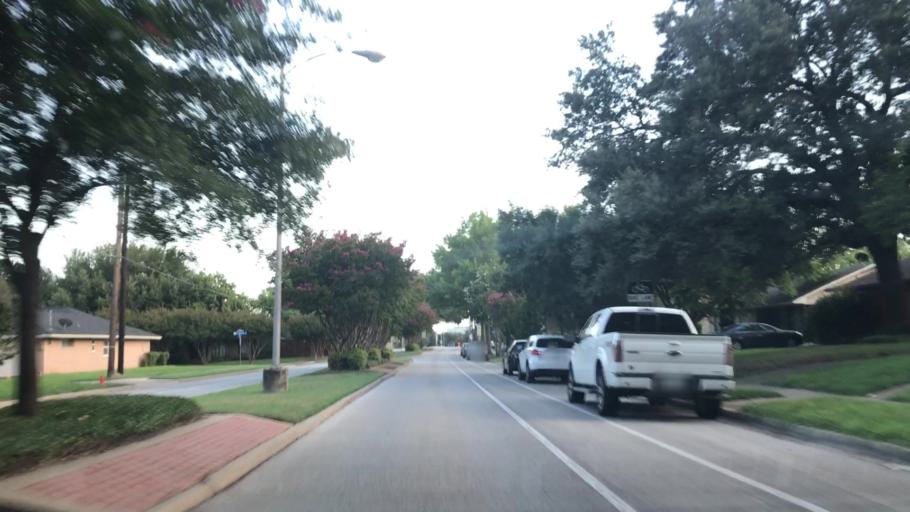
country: US
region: Texas
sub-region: Dallas County
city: Richardson
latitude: 32.9450
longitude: -96.7574
